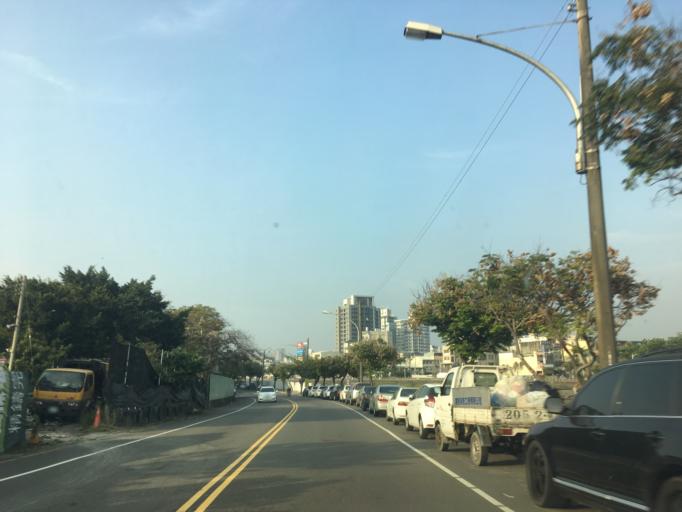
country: TW
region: Taiwan
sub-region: Taichung City
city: Taichung
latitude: 24.1657
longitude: 120.7050
